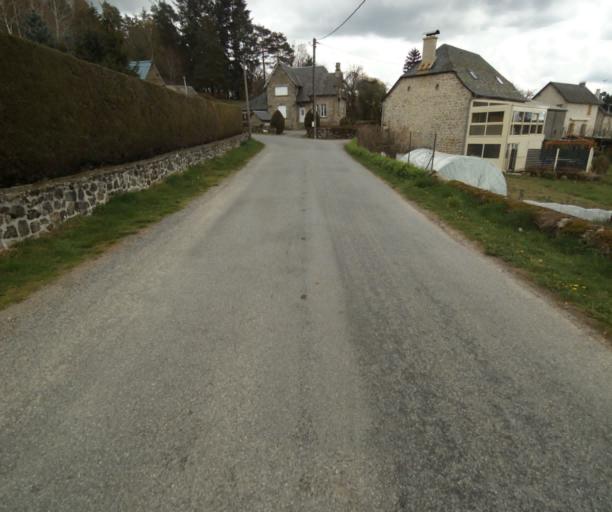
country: FR
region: Limousin
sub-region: Departement de la Correze
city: Correze
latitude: 45.3171
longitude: 1.9269
